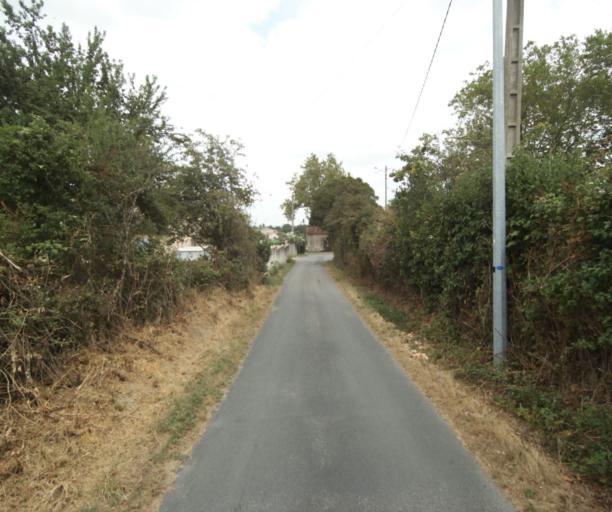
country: FR
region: Midi-Pyrenees
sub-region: Departement de la Haute-Garonne
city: Revel
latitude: 43.4485
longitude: 2.0062
